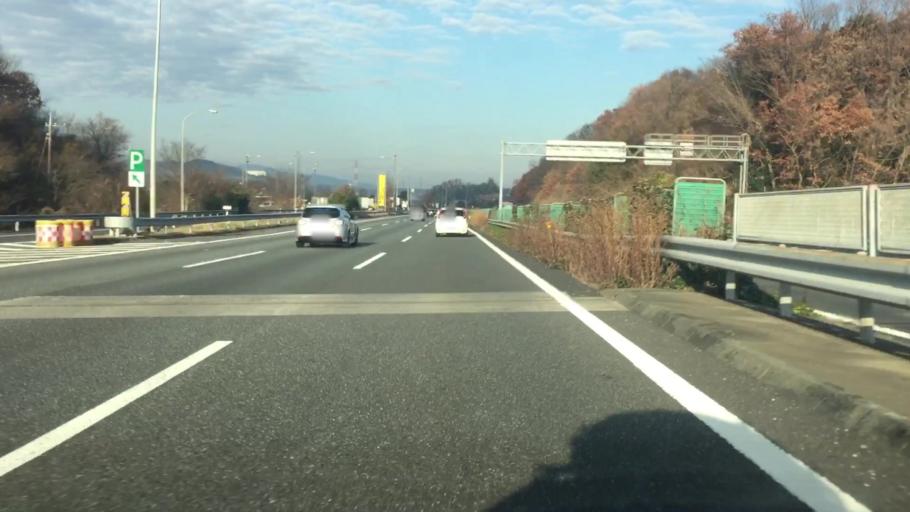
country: JP
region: Saitama
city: Ogawa
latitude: 36.0850
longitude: 139.2937
